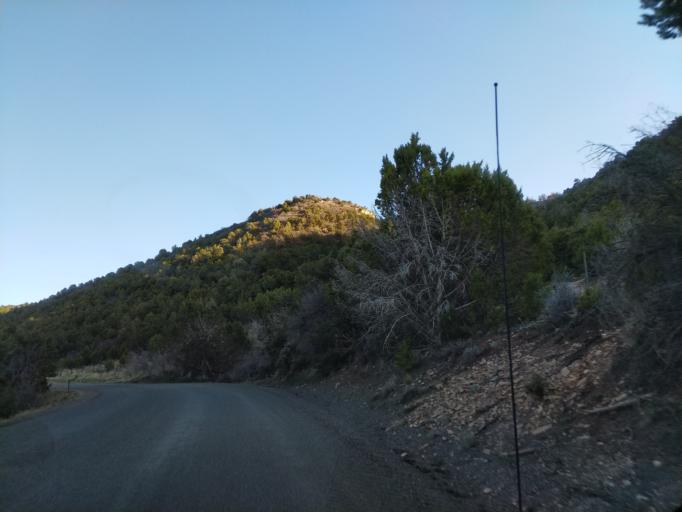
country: US
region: Colorado
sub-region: Mesa County
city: Loma
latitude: 38.9540
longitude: -108.9961
